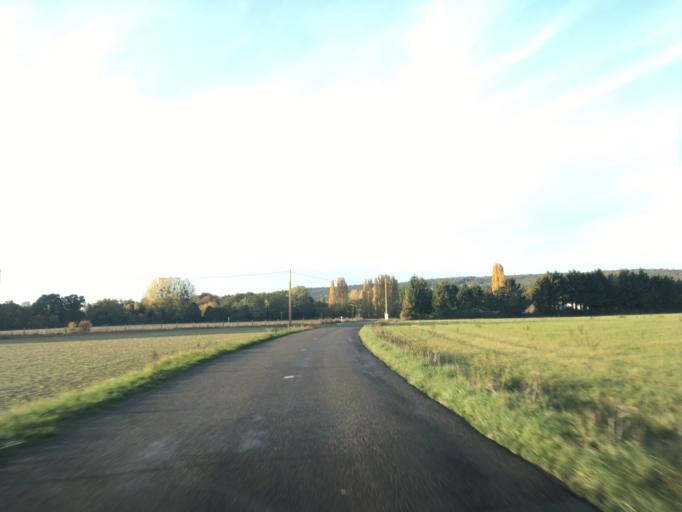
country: FR
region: Haute-Normandie
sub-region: Departement de l'Eure
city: Heudreville-sur-Eure
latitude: 49.1202
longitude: 1.2153
